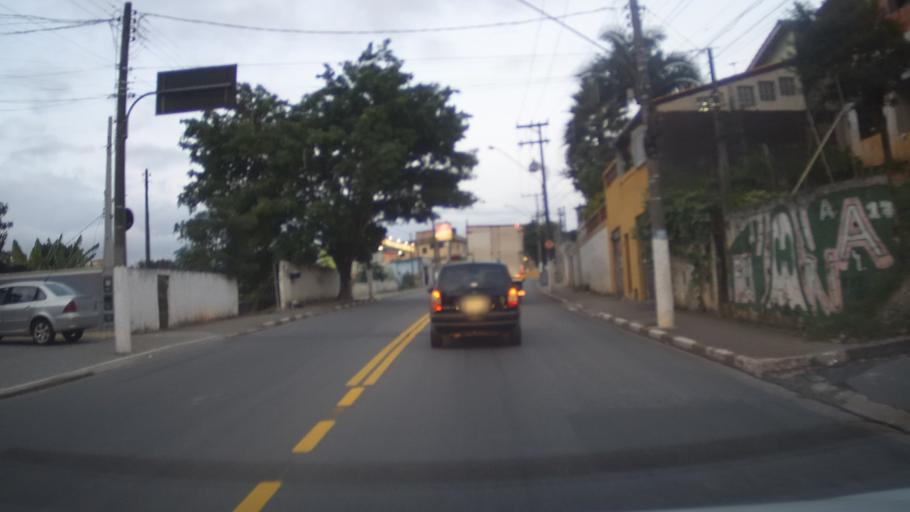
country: BR
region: Sao Paulo
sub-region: Aruja
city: Aruja
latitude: -23.3891
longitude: -46.3152
